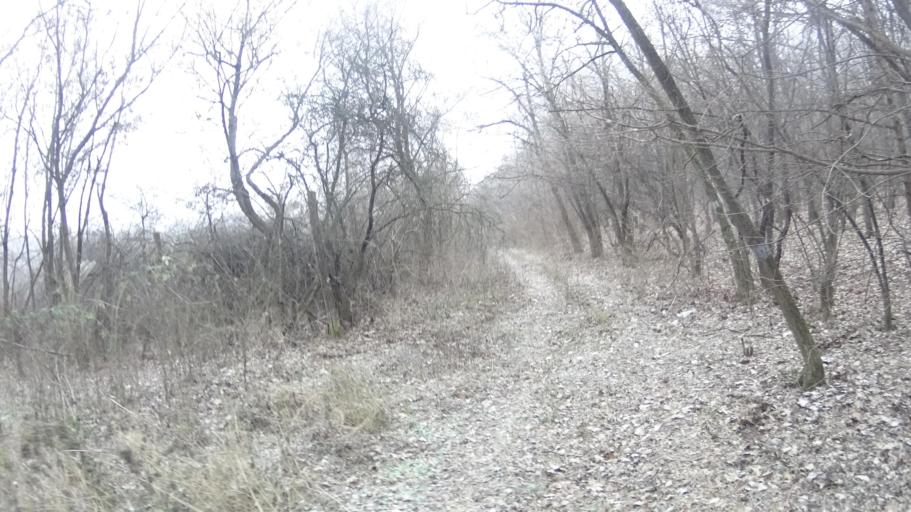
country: HU
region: Pest
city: Kosd
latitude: 47.8091
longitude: 19.1913
